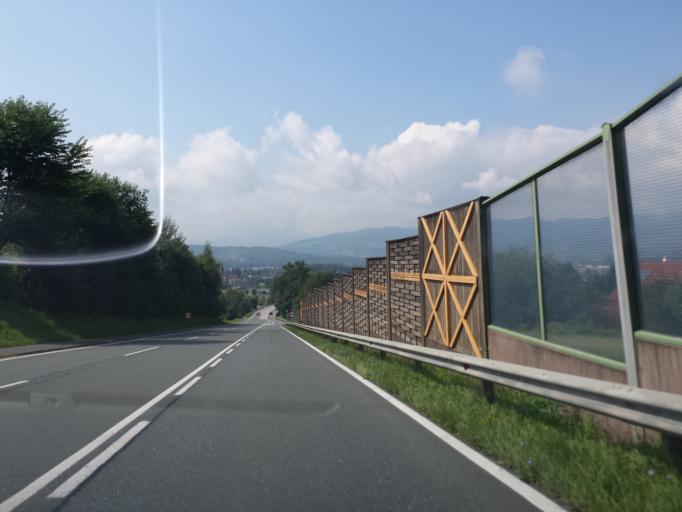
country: AT
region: Styria
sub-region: Politischer Bezirk Deutschlandsberg
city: Rassach
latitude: 46.8345
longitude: 15.2627
